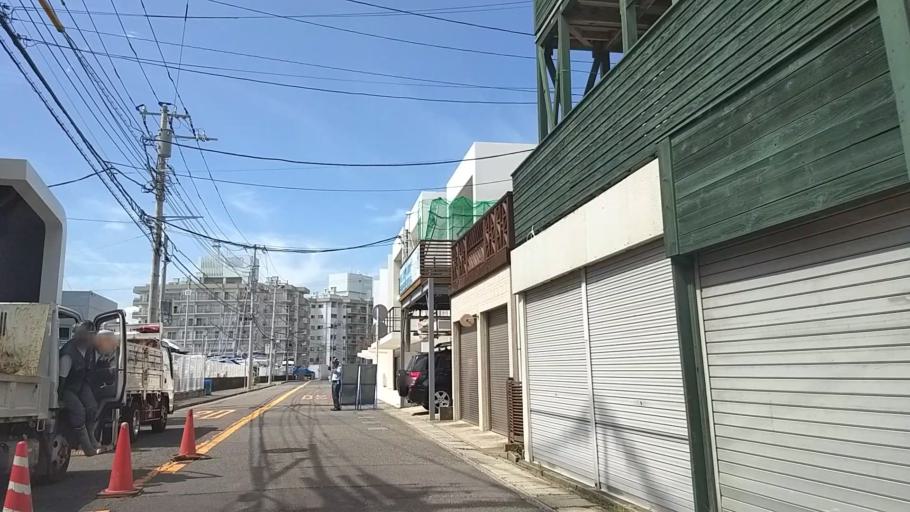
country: JP
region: Kanagawa
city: Hayama
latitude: 35.2276
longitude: 139.6040
